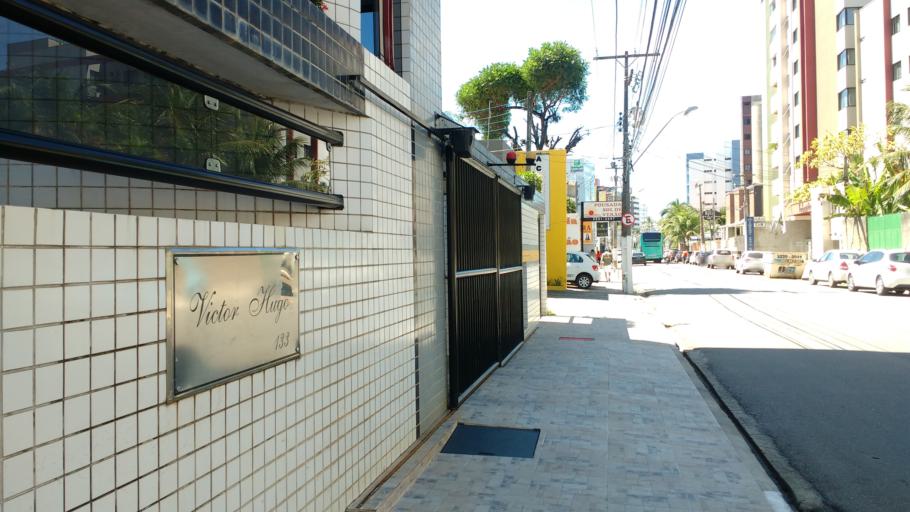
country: BR
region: Alagoas
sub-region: Maceio
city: Maceio
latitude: -9.6627
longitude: -35.7080
